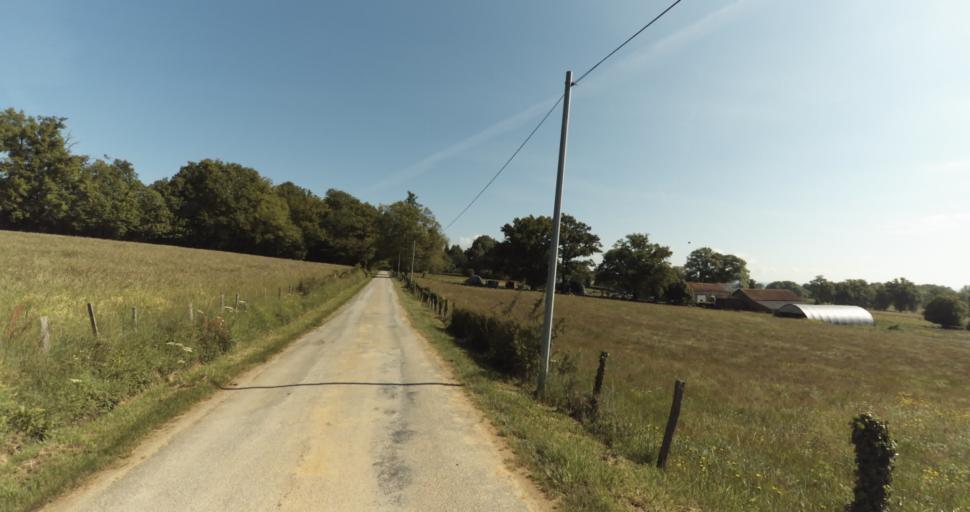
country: FR
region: Limousin
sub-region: Departement de la Haute-Vienne
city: Solignac
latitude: 45.7161
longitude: 1.2660
